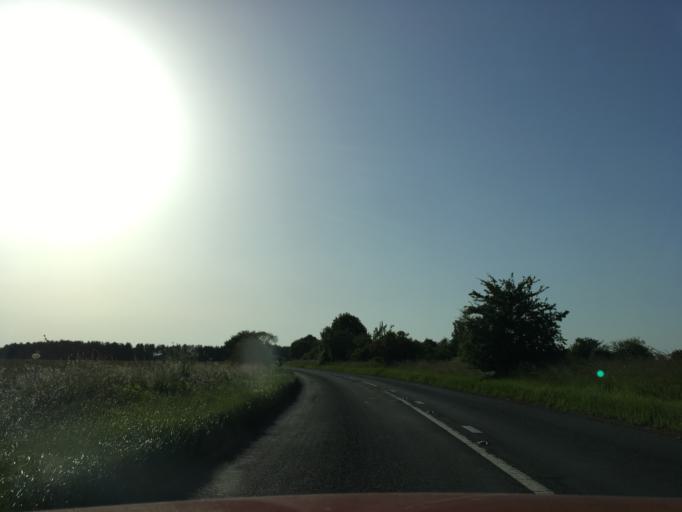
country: GB
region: England
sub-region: Gloucestershire
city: Fairford
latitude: 51.7053
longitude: -1.8456
